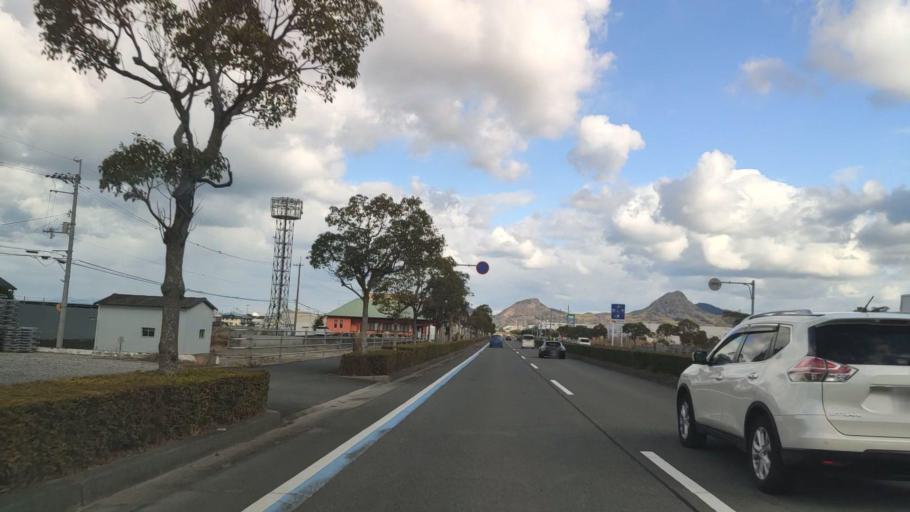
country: JP
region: Ehime
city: Hojo
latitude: 33.9572
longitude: 132.7764
